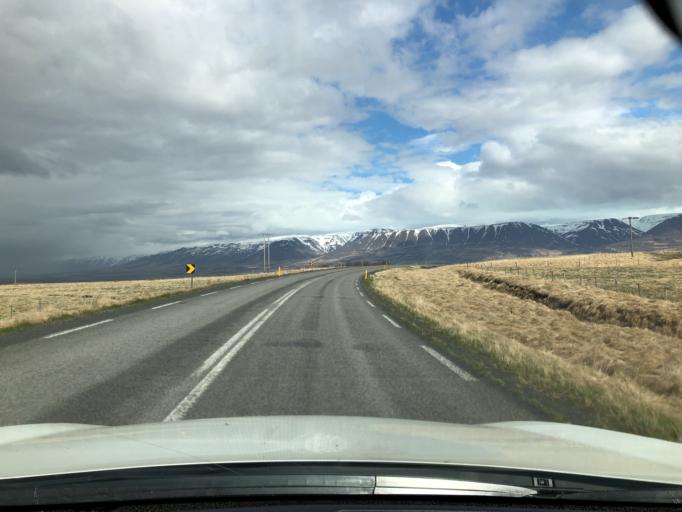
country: IS
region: Northwest
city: Saudarkrokur
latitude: 65.5475
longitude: -19.4913
